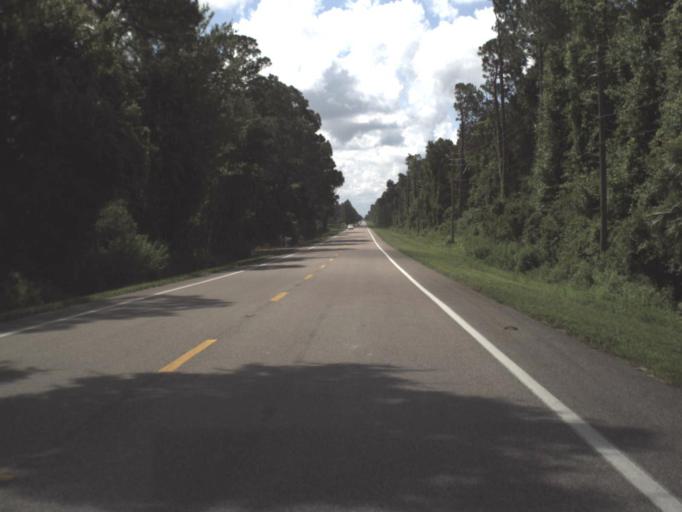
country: US
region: Florida
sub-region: Putnam County
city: East Palatka
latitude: 29.5956
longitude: -81.5712
